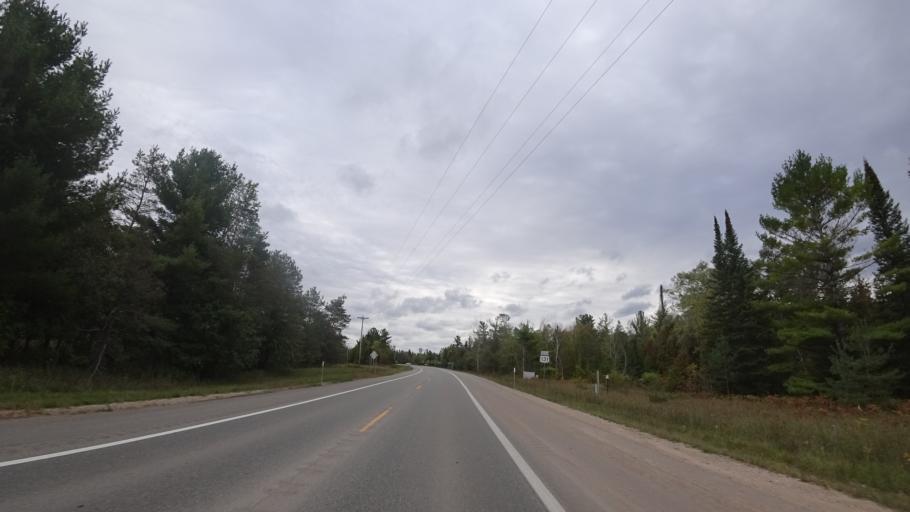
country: US
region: Michigan
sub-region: Charlevoix County
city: Boyne City
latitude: 45.1607
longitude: -84.9191
